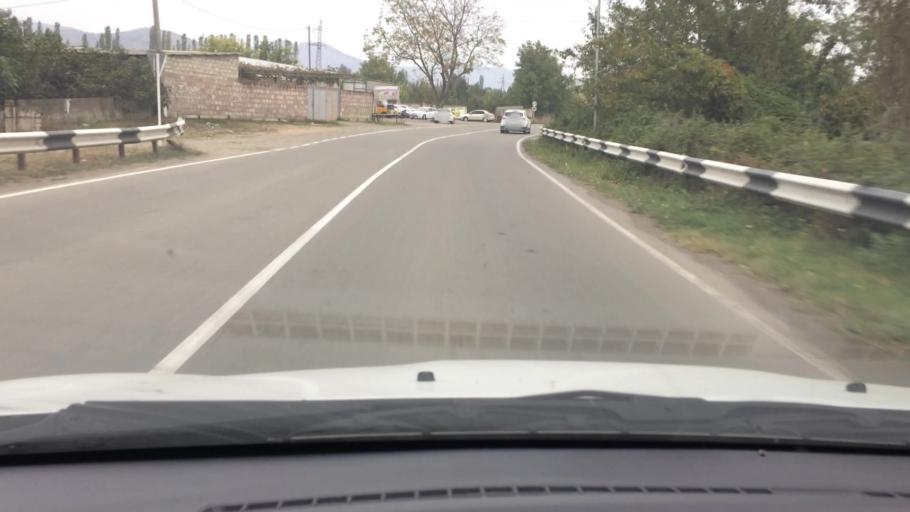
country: AM
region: Tavush
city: Bagratashen
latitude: 41.2557
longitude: 44.7985
